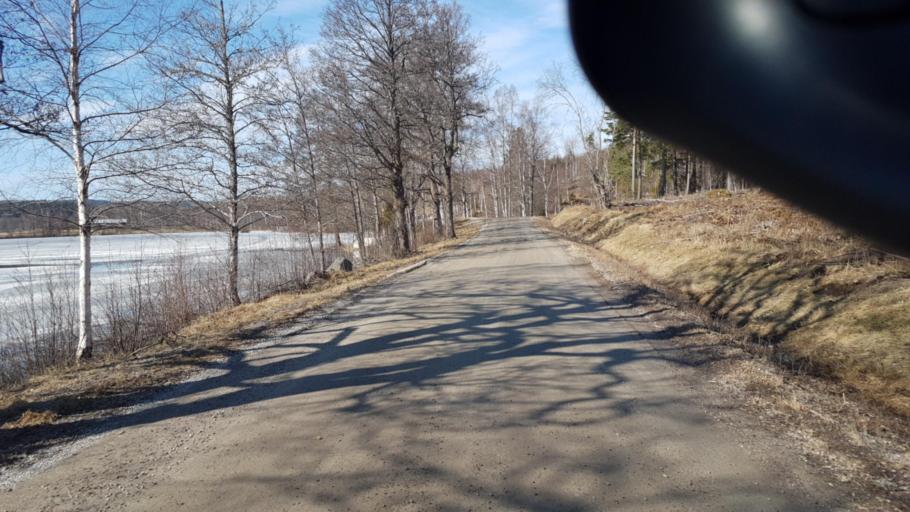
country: SE
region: Vaermland
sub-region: Arvika Kommun
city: Arvika
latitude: 59.7101
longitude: 12.8522
